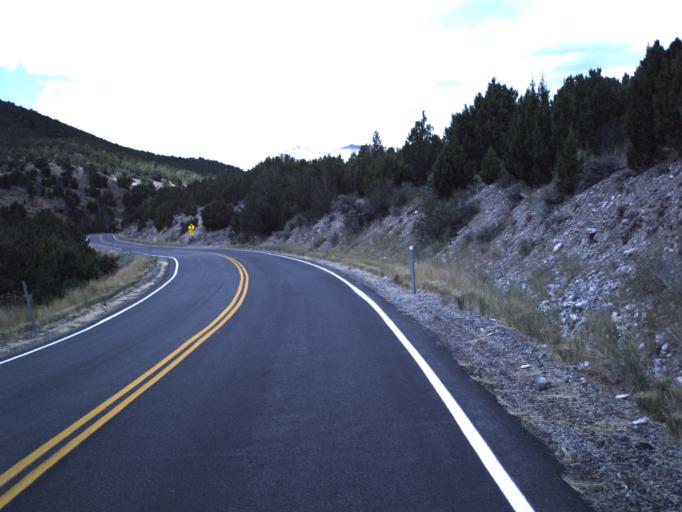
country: US
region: Utah
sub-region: Tooele County
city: Grantsville
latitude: 40.3462
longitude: -112.5497
